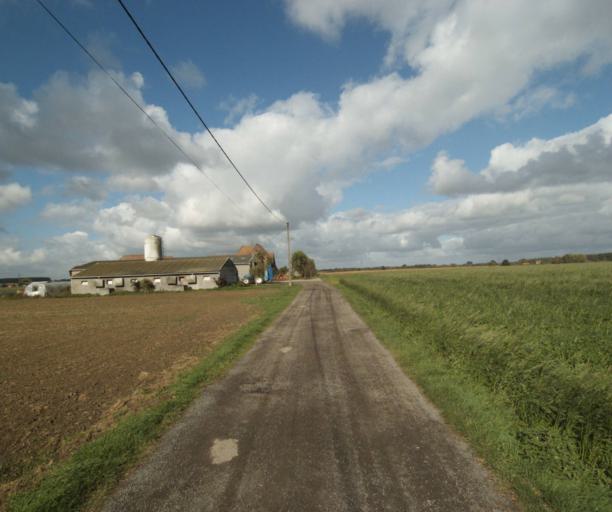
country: FR
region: Nord-Pas-de-Calais
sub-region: Departement du Nord
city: Deulemont
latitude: 50.7106
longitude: 2.9639
